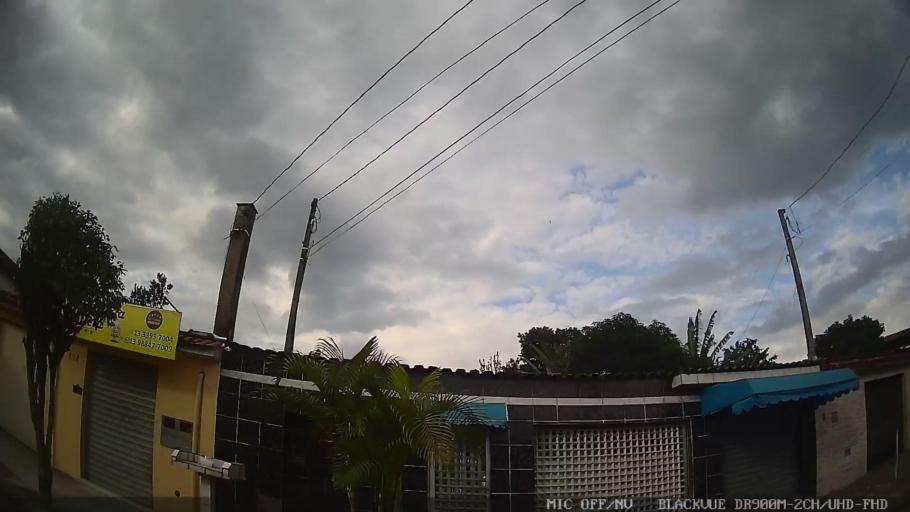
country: BR
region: Sao Paulo
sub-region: Guaruja
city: Guaruja
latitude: -23.9793
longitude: -46.2351
